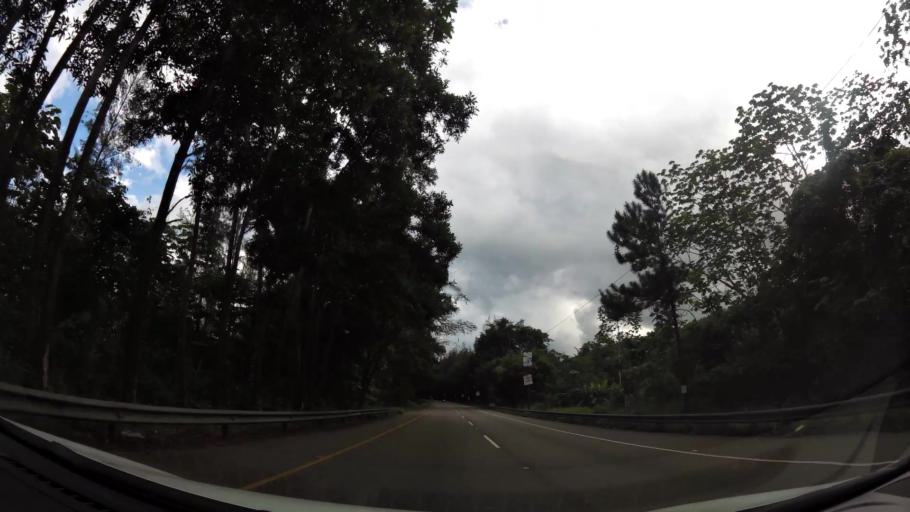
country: DO
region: La Vega
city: Rincon
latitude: 19.1268
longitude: -70.4543
